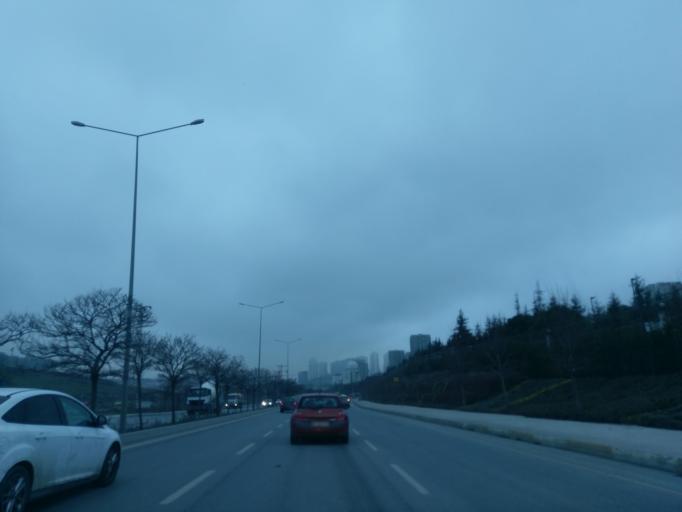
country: TR
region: Istanbul
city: Mahmutbey
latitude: 41.0438
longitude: 28.7739
